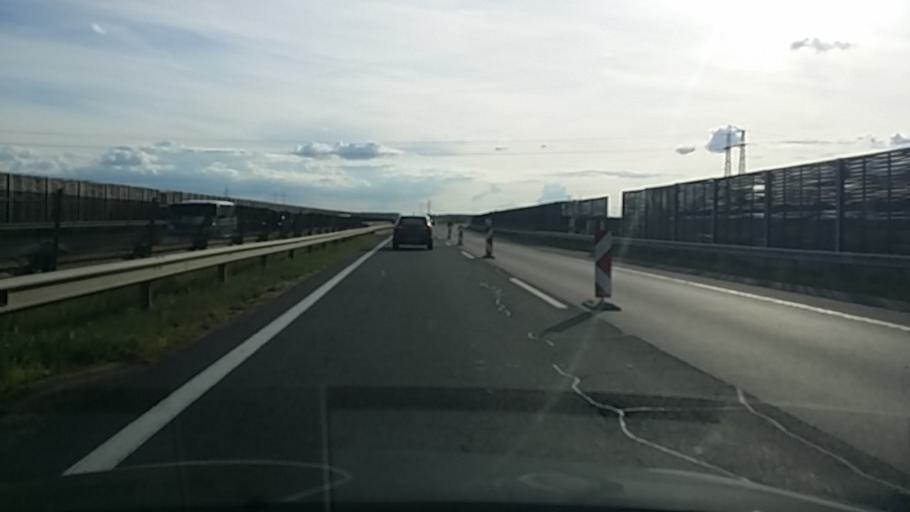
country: HU
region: Hajdu-Bihar
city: Polgar
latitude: 47.8485
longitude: 21.1316
